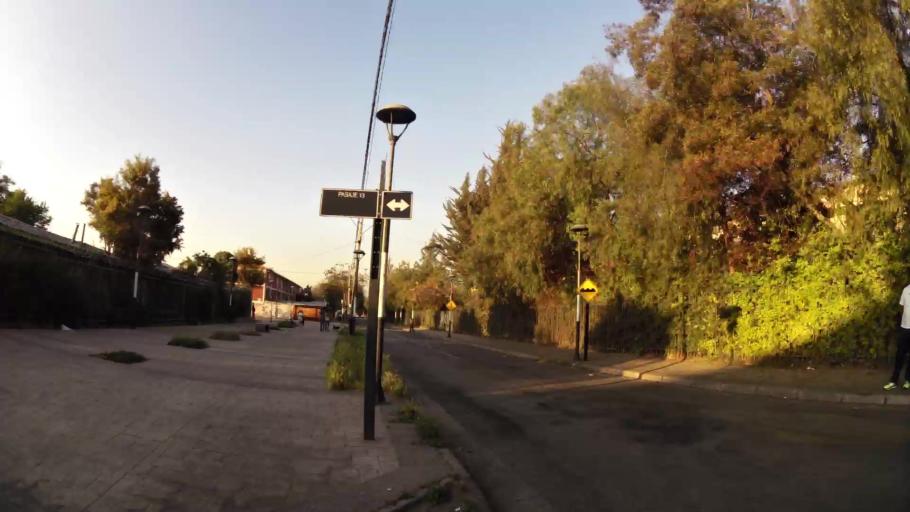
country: CL
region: Santiago Metropolitan
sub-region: Provincia de Santiago
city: Santiago
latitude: -33.5172
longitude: -70.6175
